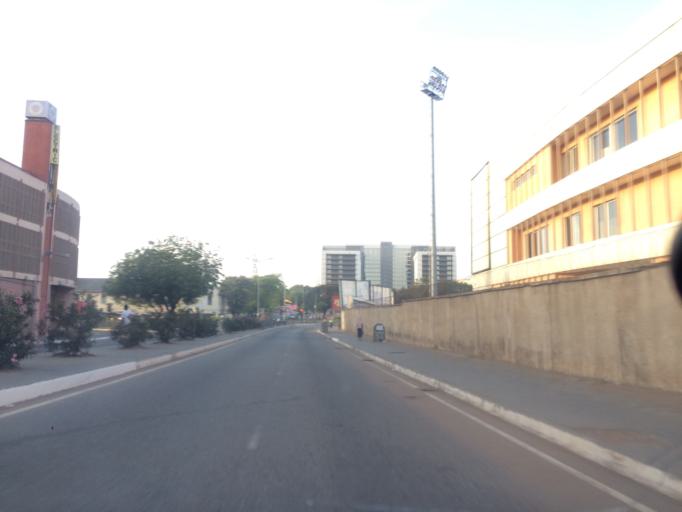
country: GH
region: Greater Accra
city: Accra
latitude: 5.5477
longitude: -0.2035
